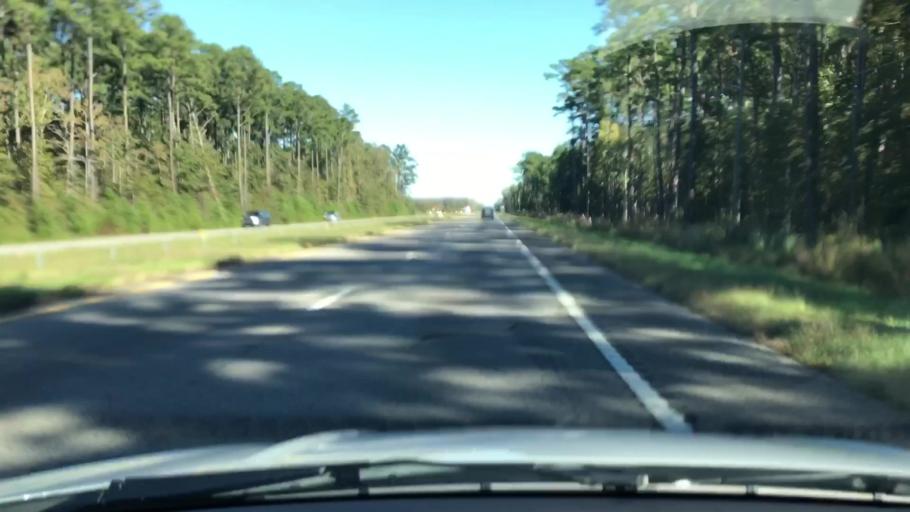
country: US
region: South Carolina
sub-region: Colleton County
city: Walterboro
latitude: 32.7655
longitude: -80.5039
